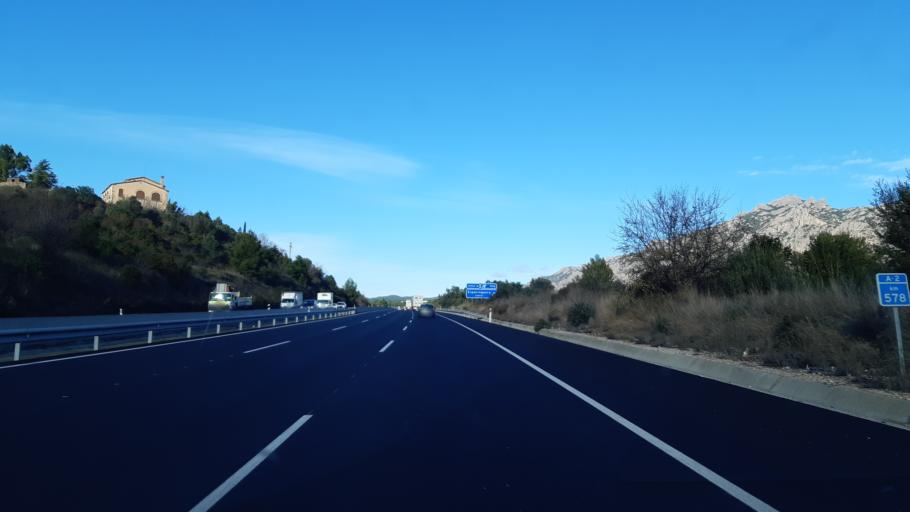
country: ES
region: Catalonia
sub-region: Provincia de Barcelona
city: Esparreguera
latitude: 41.5479
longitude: 1.8507
